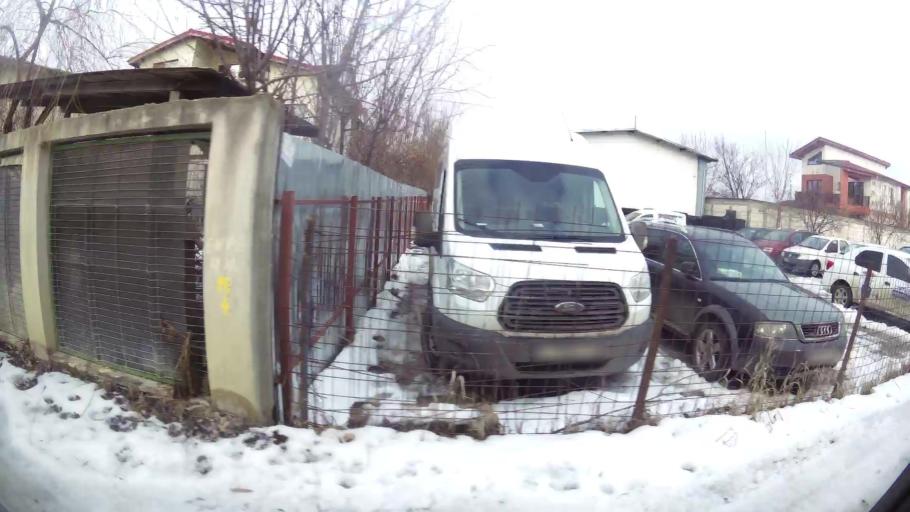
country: RO
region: Ilfov
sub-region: Comuna Popesti-Leordeni
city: Popesti-Leordeni
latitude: 44.4044
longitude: 26.1841
